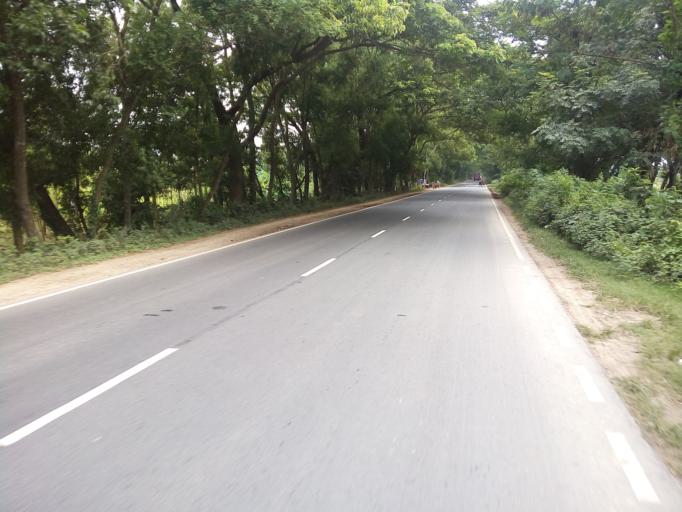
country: BD
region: Khulna
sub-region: Magura
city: Magura
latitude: 23.5343
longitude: 89.6163
